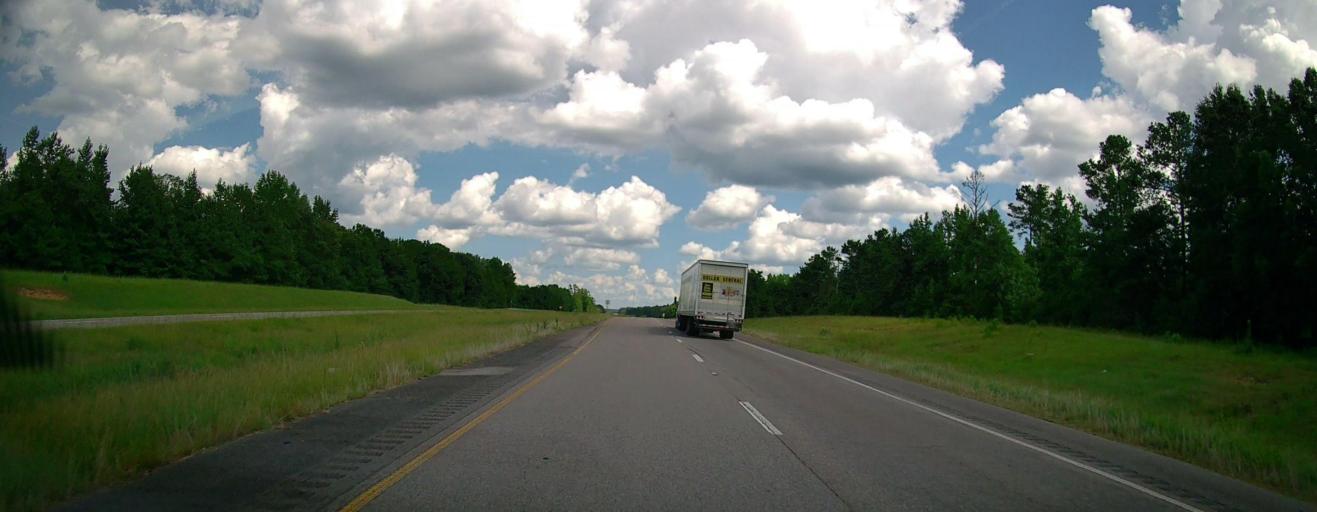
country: US
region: Mississippi
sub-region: Lowndes County
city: New Hope
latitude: 33.4876
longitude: -88.2692
